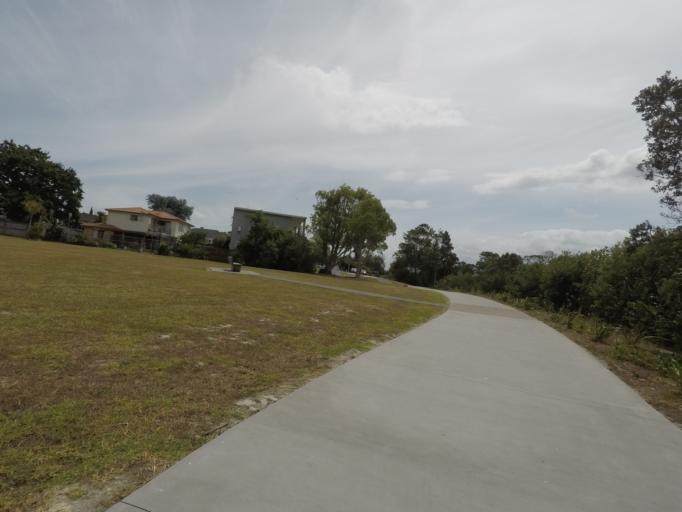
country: NZ
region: Auckland
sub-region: Auckland
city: Rosebank
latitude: -36.8701
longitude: 174.6554
